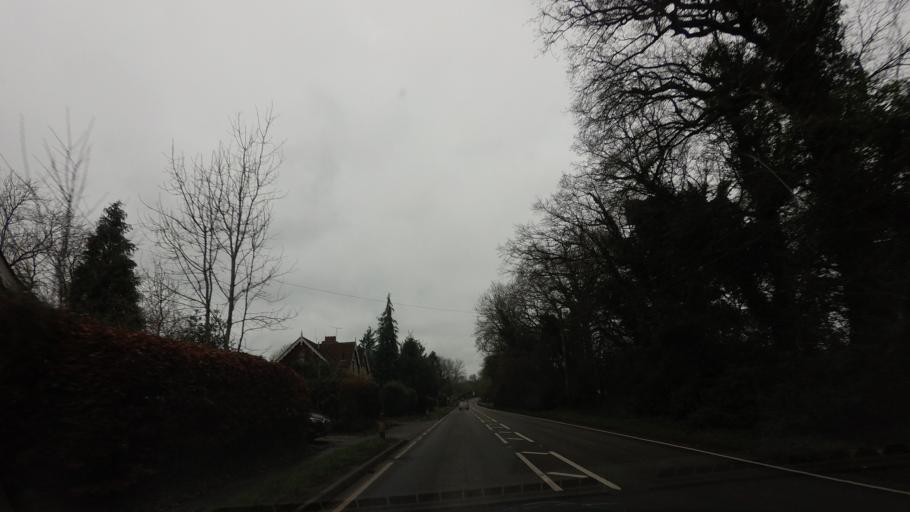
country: GB
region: England
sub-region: Kent
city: Marden
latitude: 51.2161
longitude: 0.5121
